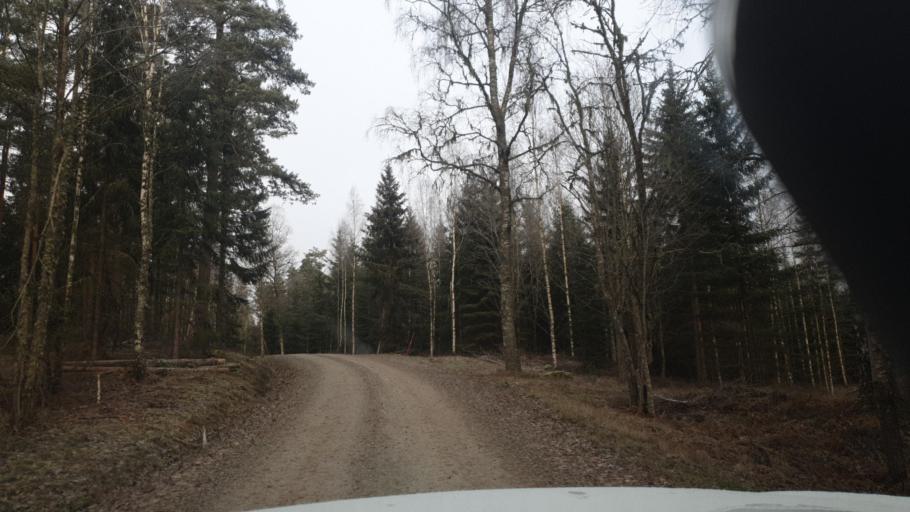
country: SE
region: Vaermland
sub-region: Karlstads Kommun
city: Valberg
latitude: 59.4522
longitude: 13.0941
